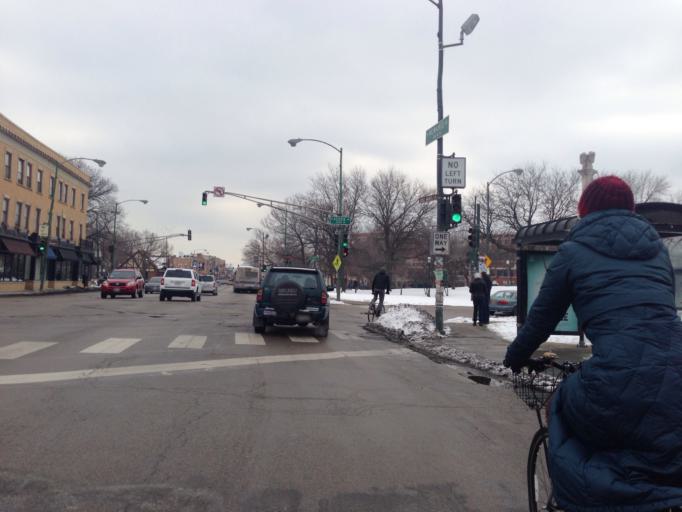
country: US
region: Illinois
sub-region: Cook County
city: Lincolnwood
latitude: 41.9293
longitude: -87.7078
